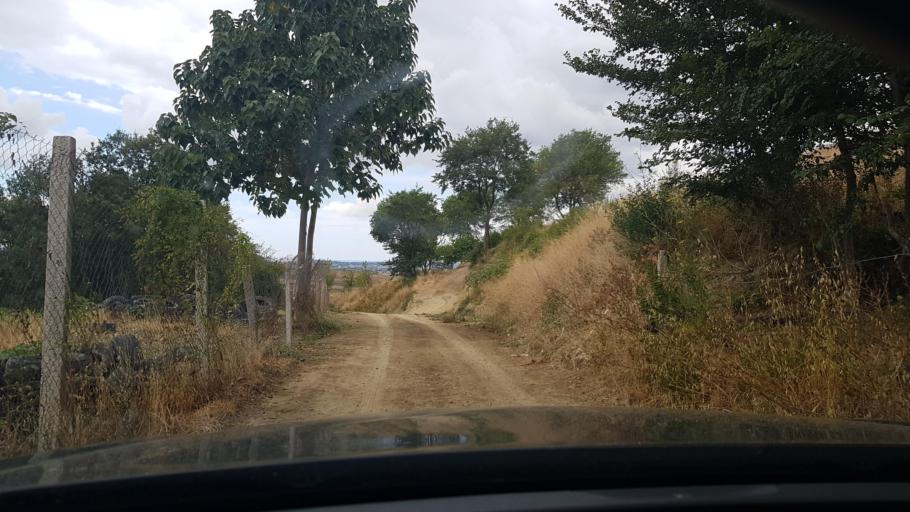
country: AL
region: Durres
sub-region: Rrethi i Durresit
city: Gjepalaj
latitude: 41.3008
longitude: 19.5549
